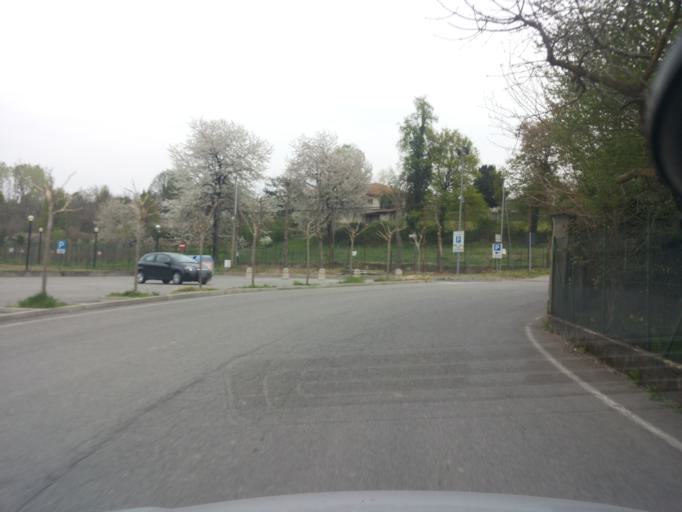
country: IT
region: Piedmont
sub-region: Provincia di Torino
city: Caravino
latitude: 45.4011
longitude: 7.9617
